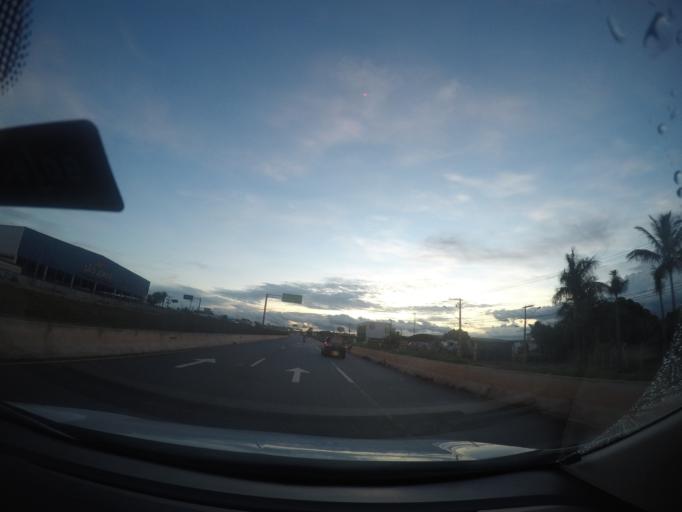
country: BR
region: Goias
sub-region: Goiania
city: Goiania
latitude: -16.7155
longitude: -49.3631
